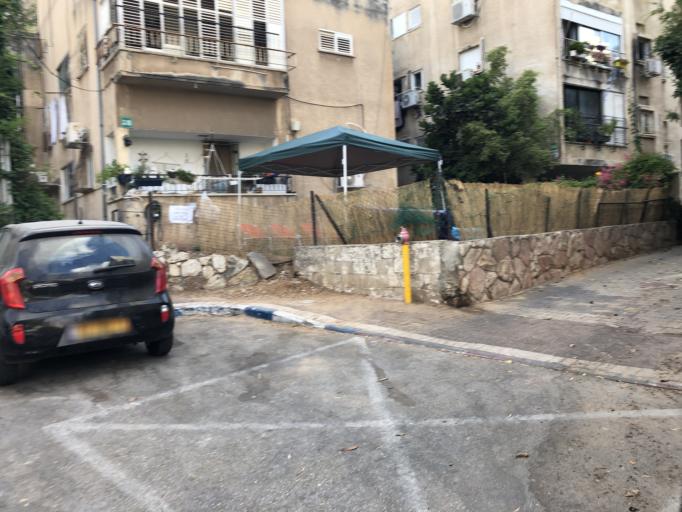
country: IL
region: Tel Aviv
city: Ramat Gan
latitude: 32.0812
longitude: 34.8195
